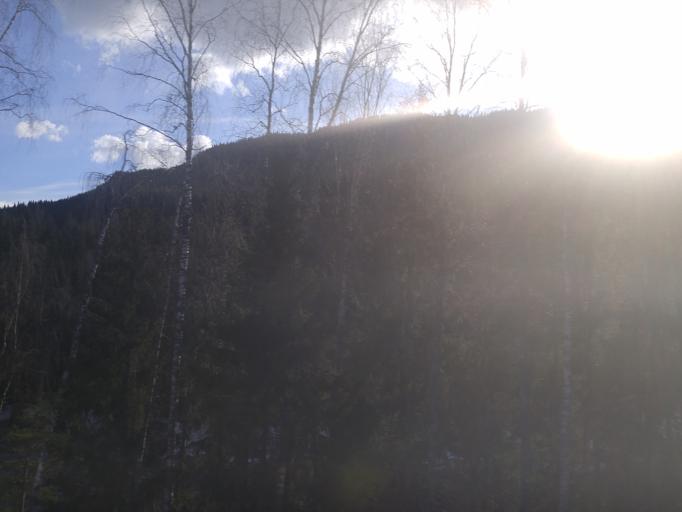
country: NO
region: Oppland
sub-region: Lillehammer
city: Lillehammer
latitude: 61.1913
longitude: 10.4117
